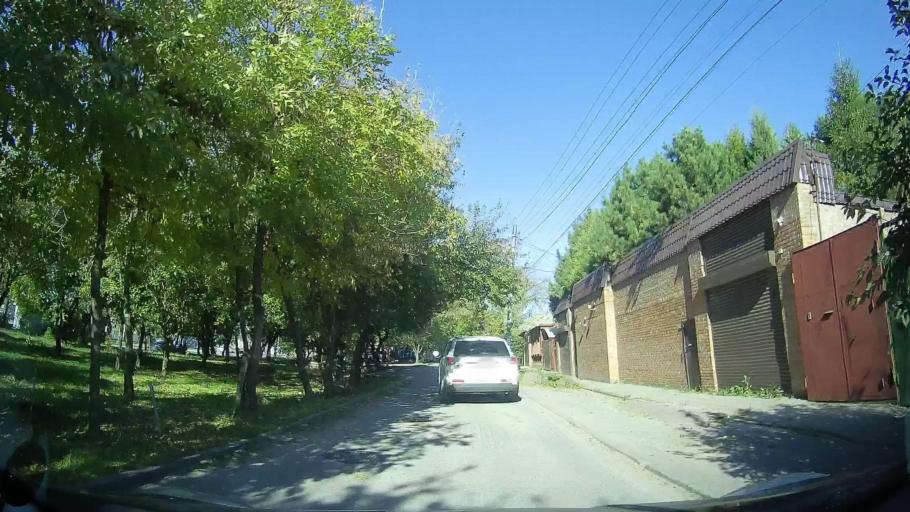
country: RU
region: Rostov
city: Rostov-na-Donu
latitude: 47.2405
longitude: 39.6724
